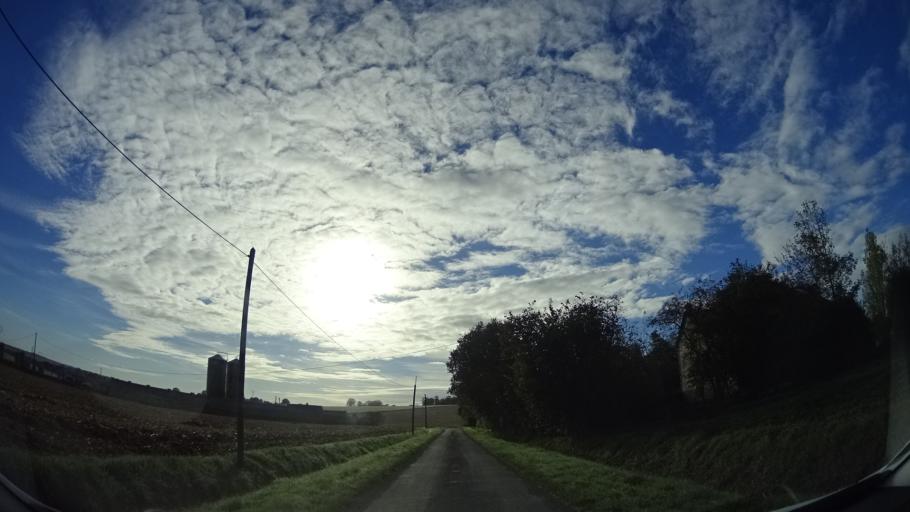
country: FR
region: Brittany
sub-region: Departement d'Ille-et-Vilaine
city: Geveze
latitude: 48.1999
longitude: -1.8131
